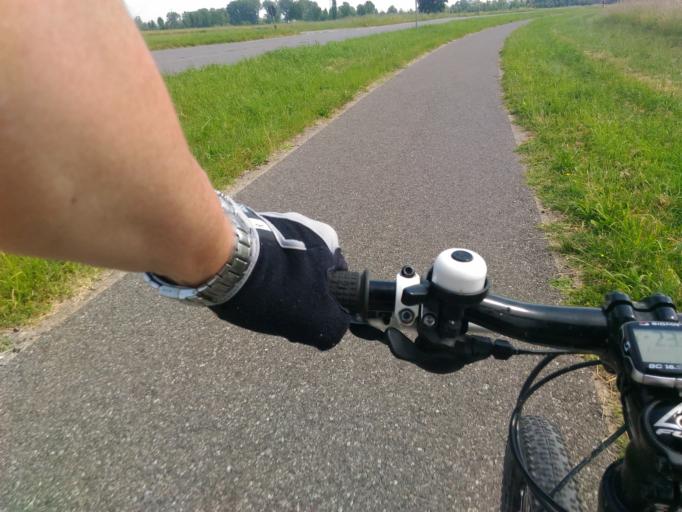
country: IT
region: Lombardy
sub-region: Provincia di Lodi
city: Mulazzano
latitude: 45.3753
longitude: 9.4068
